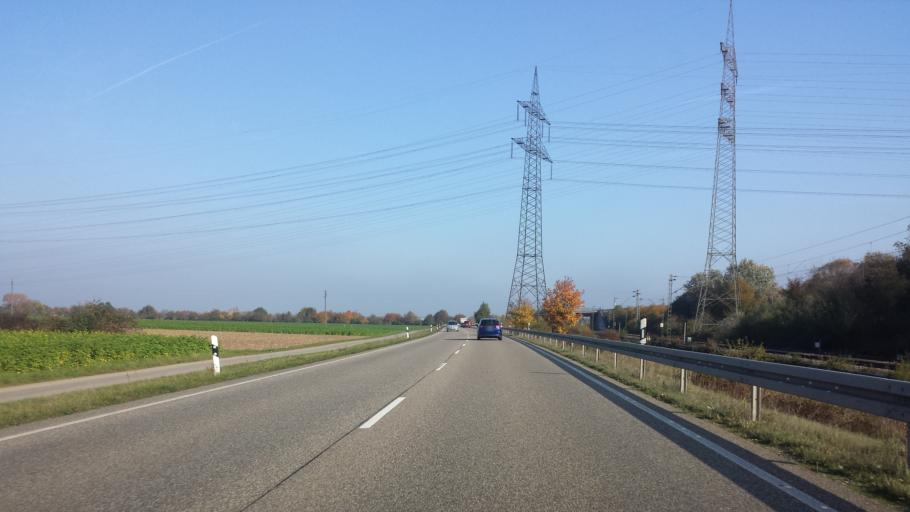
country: DE
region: Baden-Wuerttemberg
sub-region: Karlsruhe Region
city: Ubstadt-Weiher
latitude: 49.1540
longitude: 8.6123
